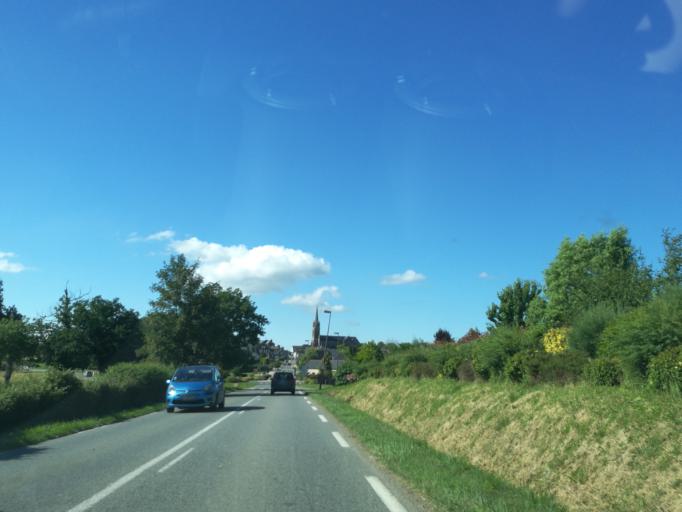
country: FR
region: Brittany
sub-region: Departement d'Ille-et-Vilaine
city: Bedee
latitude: 48.1742
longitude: -1.9444
